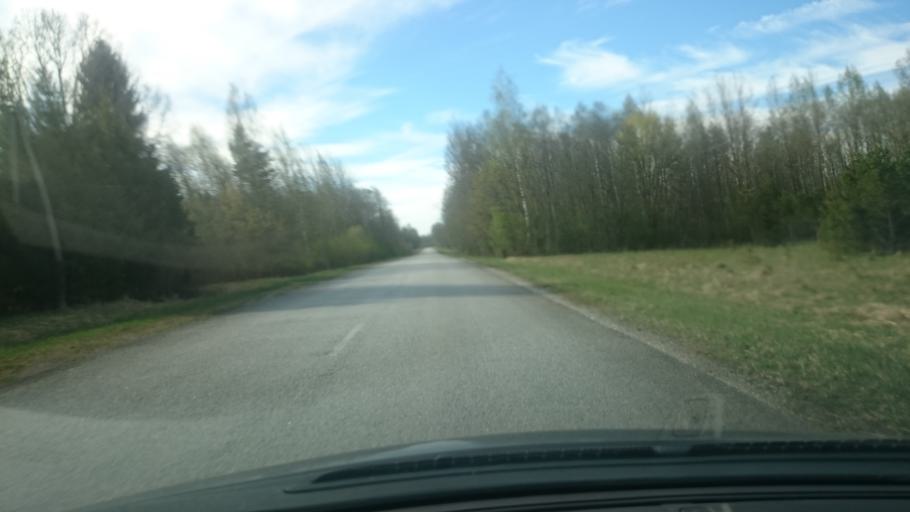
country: EE
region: Ida-Virumaa
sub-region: Sillamaee linn
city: Sillamae
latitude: 59.0882
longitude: 27.6659
